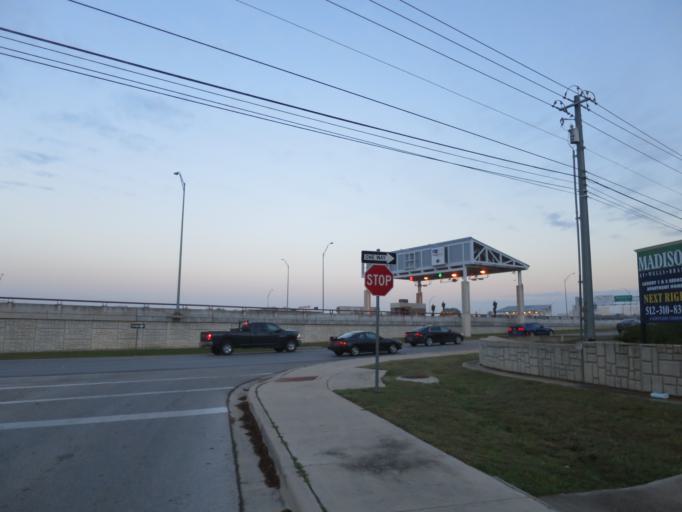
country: US
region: Texas
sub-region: Travis County
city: Wells Branch
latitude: 30.4341
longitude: -97.6987
